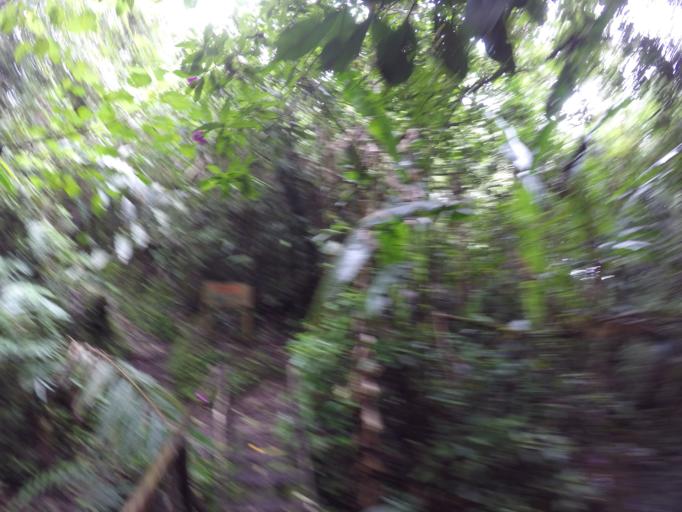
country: CO
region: Quindio
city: Filandia
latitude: 4.7123
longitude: -75.6716
